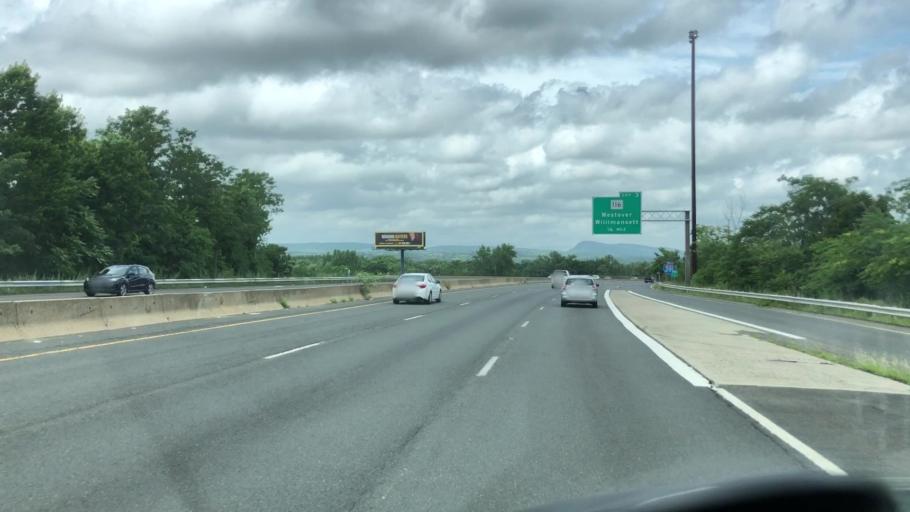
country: US
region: Massachusetts
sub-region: Hampden County
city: Chicopee
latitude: 42.1431
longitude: -72.6139
